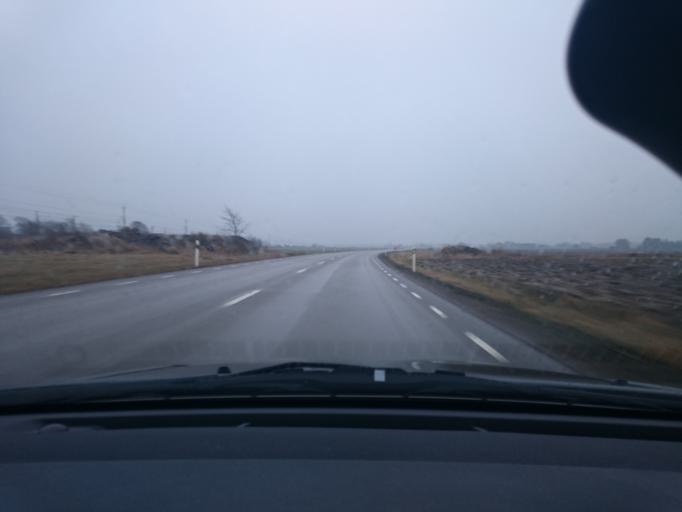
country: SE
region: Skane
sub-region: Bastads Kommun
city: Forslov
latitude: 56.3409
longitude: 12.8026
